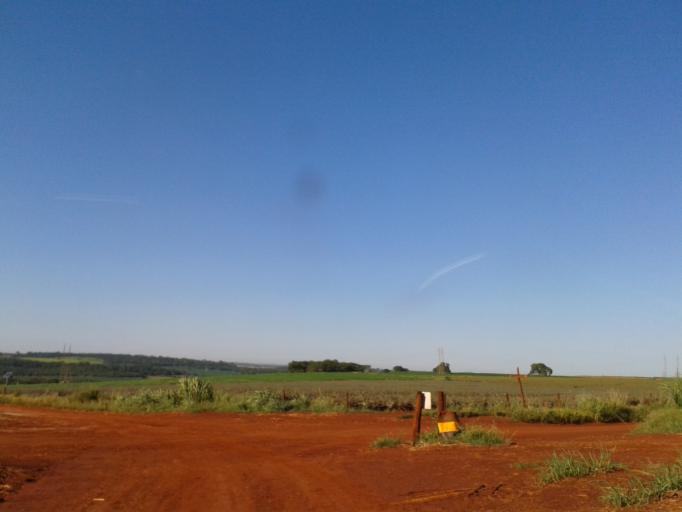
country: BR
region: Minas Gerais
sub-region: Centralina
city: Centralina
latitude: -18.6726
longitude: -49.2716
